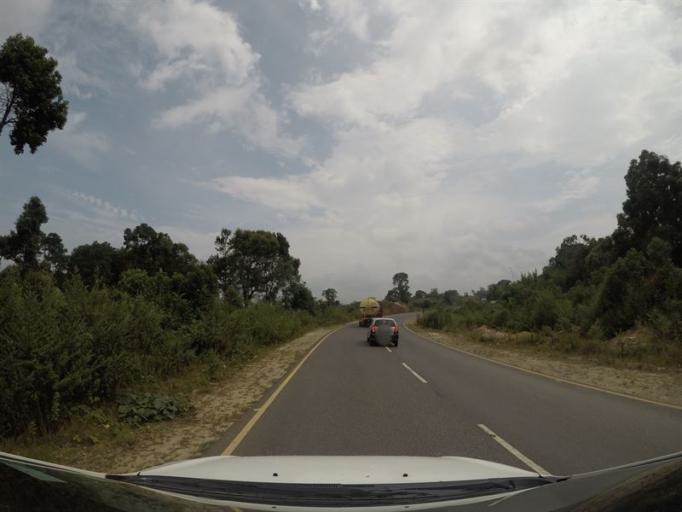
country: IN
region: Meghalaya
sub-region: East Khasi Hills
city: Shillong
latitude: 25.4881
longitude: 92.1913
